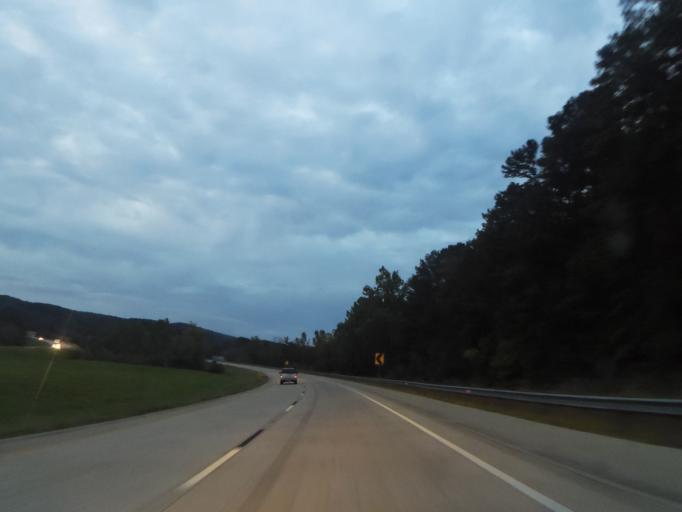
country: US
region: Alabama
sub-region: Etowah County
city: Whitesboro
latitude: 34.1200
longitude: -85.9813
